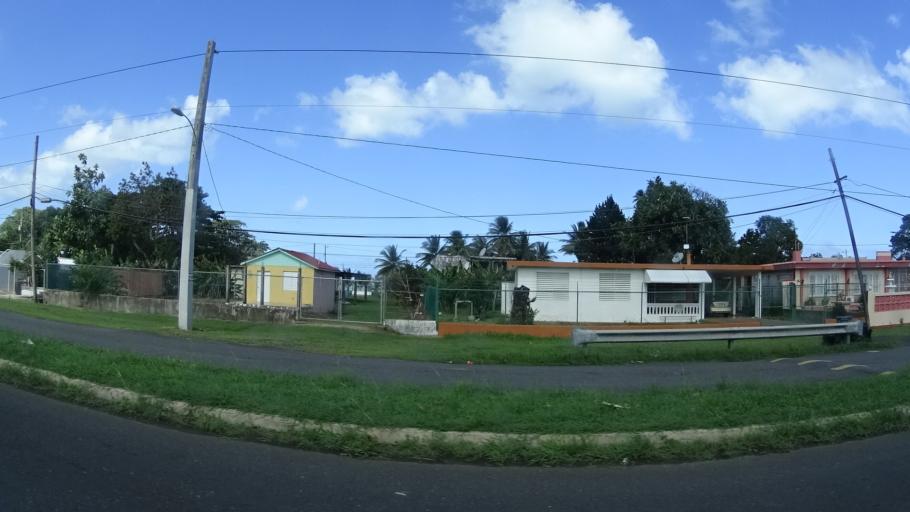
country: PR
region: Luquillo
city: Playa Fortuna
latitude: 18.3792
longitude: -65.7418
